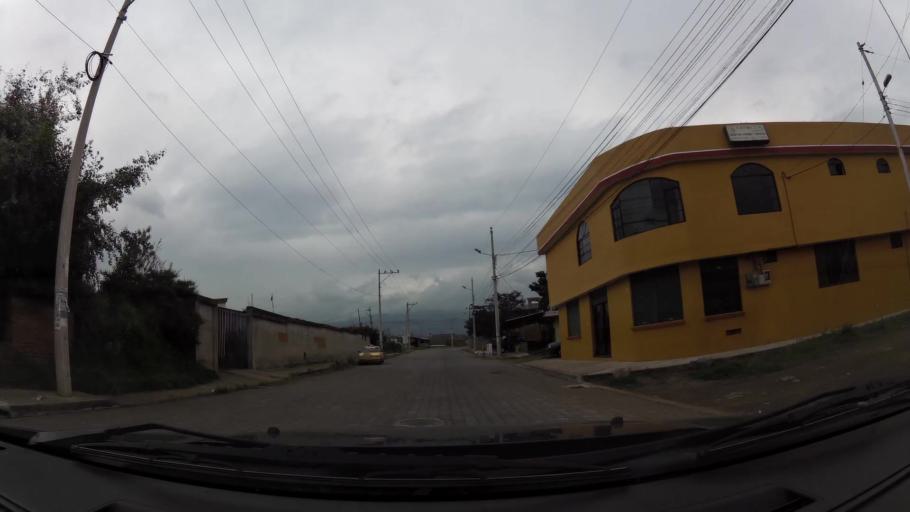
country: EC
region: Pichincha
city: Sangolqui
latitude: -0.3390
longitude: -78.4656
